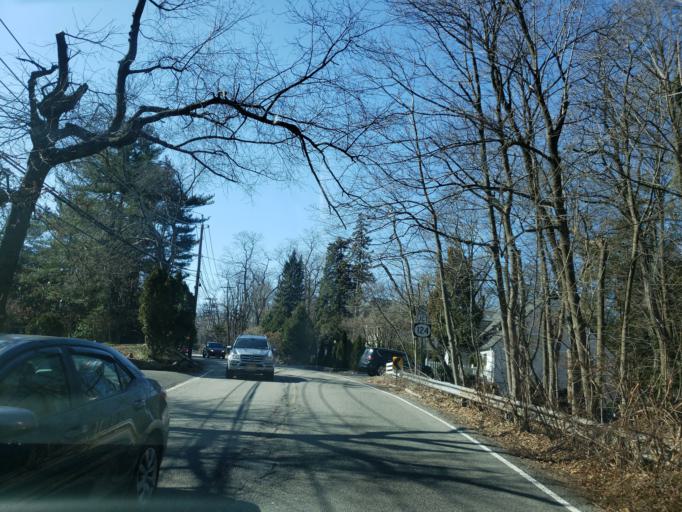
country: US
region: New Jersey
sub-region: Union County
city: Summit
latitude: 40.7282
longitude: -74.3432
